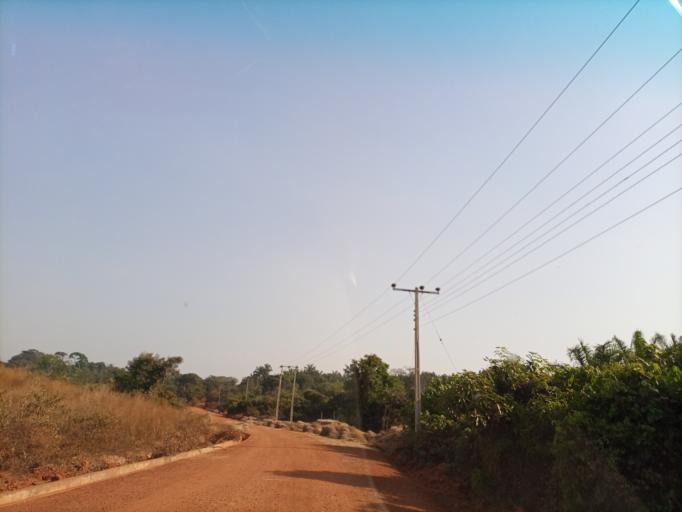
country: NG
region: Enugu
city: Opi
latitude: 6.7674
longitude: 7.3936
